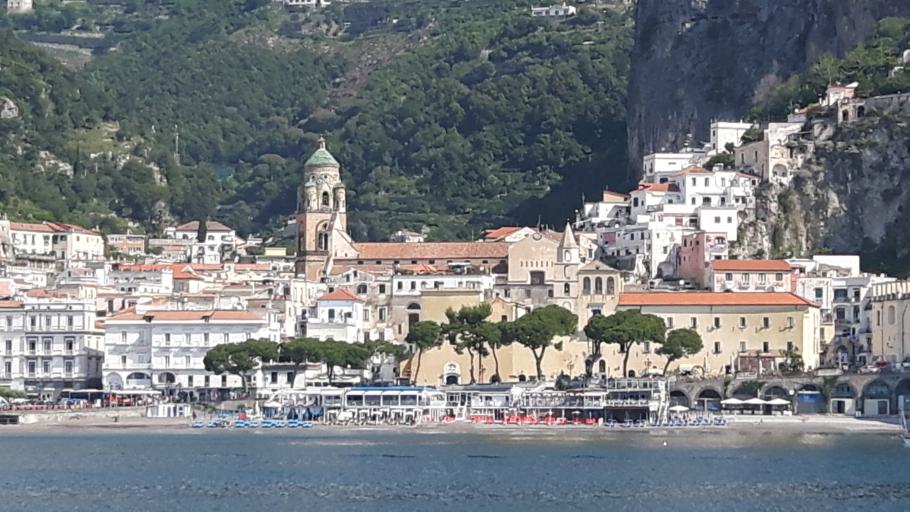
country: IT
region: Campania
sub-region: Provincia di Salerno
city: Amalfi
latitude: 40.6288
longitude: 14.6061
